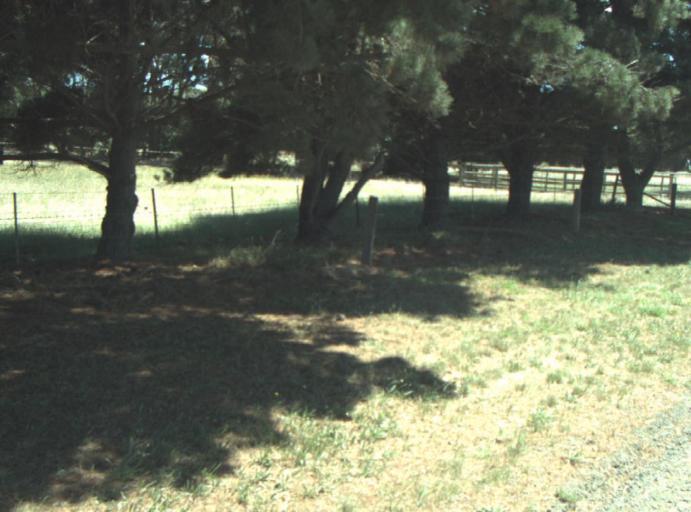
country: AU
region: Victoria
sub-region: Queenscliffe
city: Queenscliff
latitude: -38.1697
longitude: 144.7020
